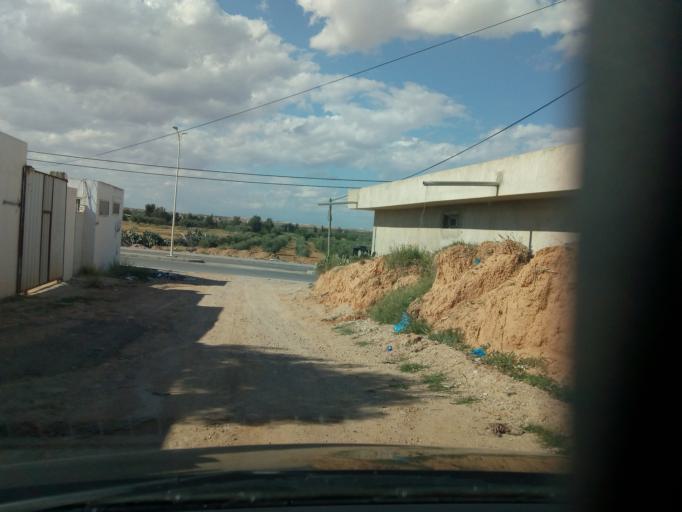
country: TN
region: Safaqis
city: Sfax
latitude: 34.7313
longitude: 10.6002
